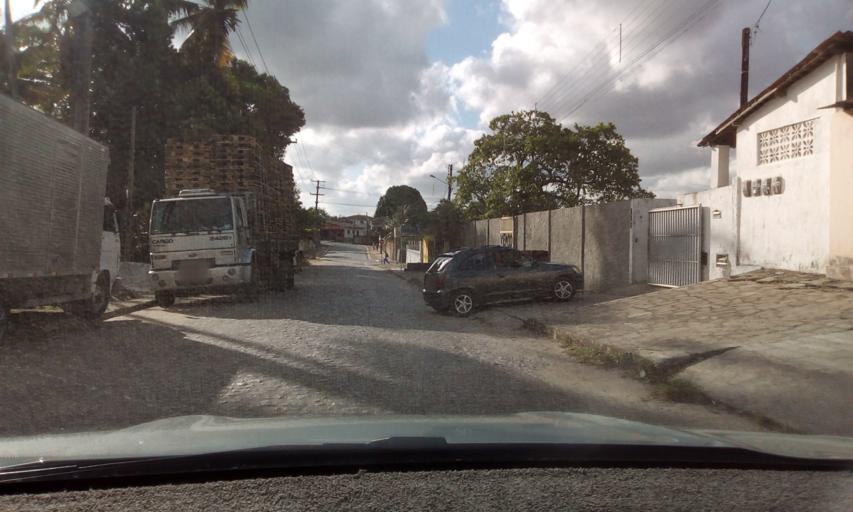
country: BR
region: Paraiba
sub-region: Bayeux
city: Bayeux
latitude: -7.1686
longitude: -34.9086
